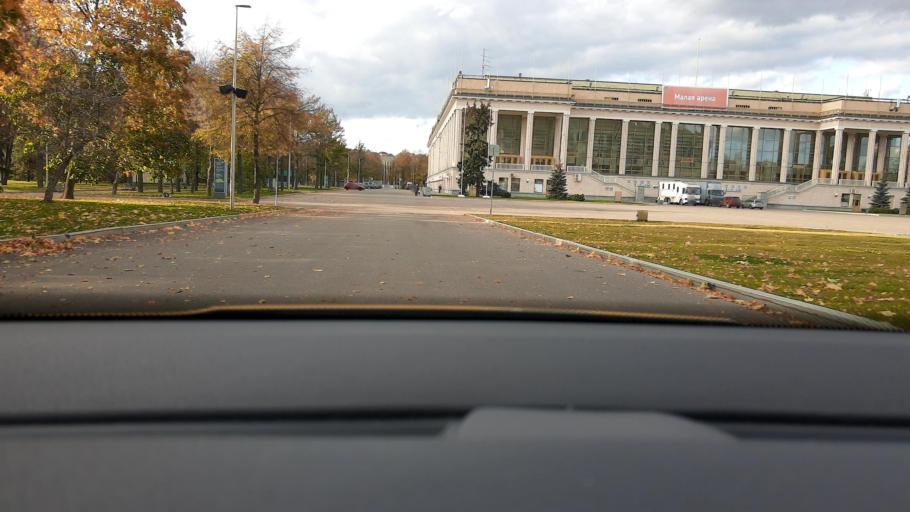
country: RU
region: Moscow
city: Luzhniki
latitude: 55.7168
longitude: 37.5509
